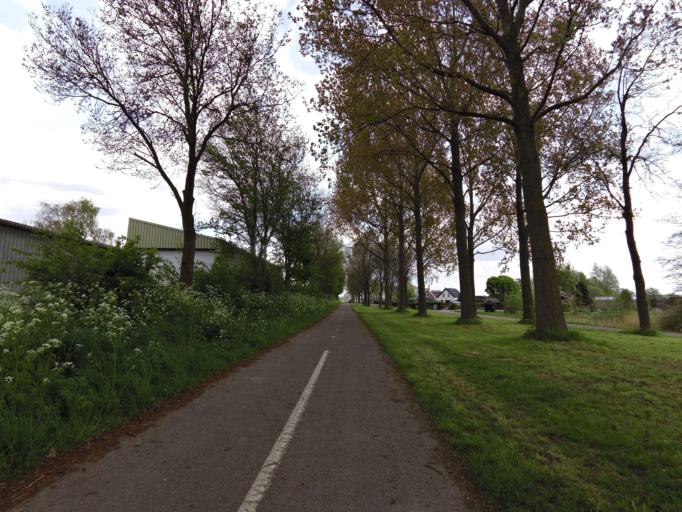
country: NL
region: South Holland
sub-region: Gemeente Hellevoetsluis
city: Nieuwenhoorn
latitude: 51.8265
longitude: 4.2187
